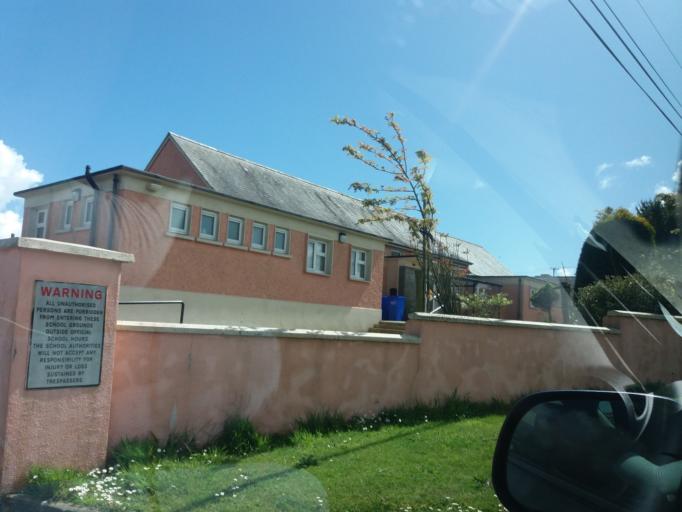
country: IE
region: Munster
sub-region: Waterford
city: Dunmore East
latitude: 52.2518
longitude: -6.9600
